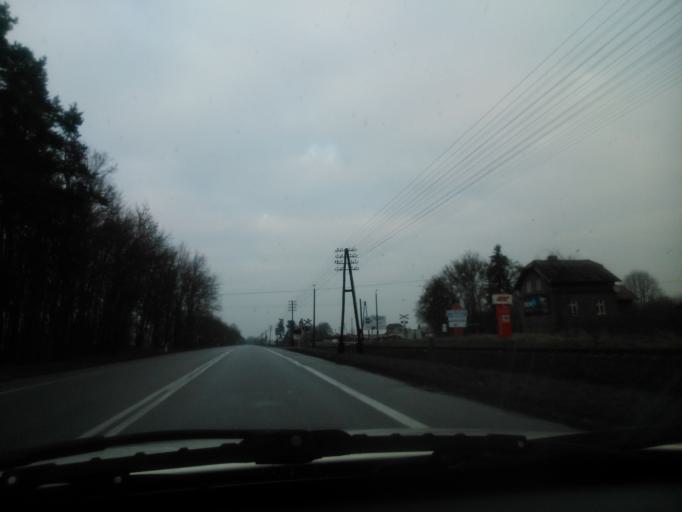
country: PL
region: Kujawsko-Pomorskie
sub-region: Powiat torunski
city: Lysomice
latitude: 53.0717
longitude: 18.6178
